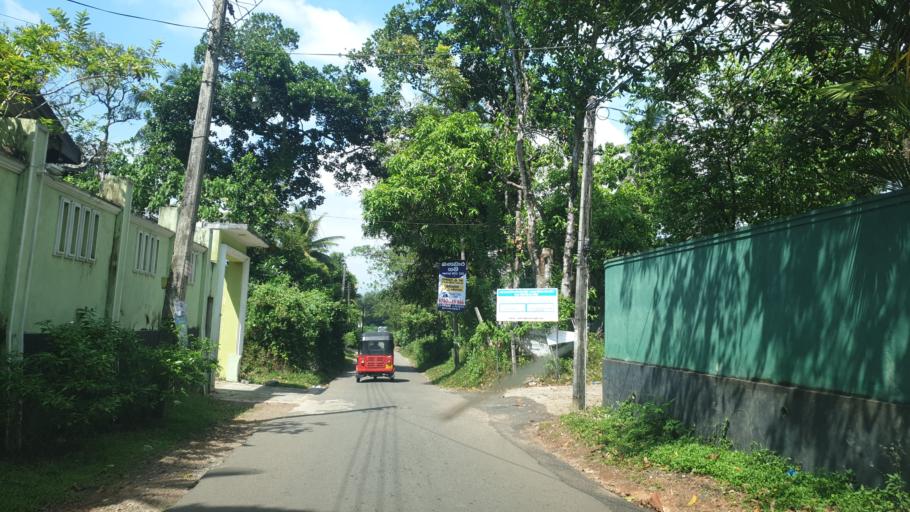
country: LK
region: Western
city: Horana South
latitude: 6.7005
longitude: 79.9862
